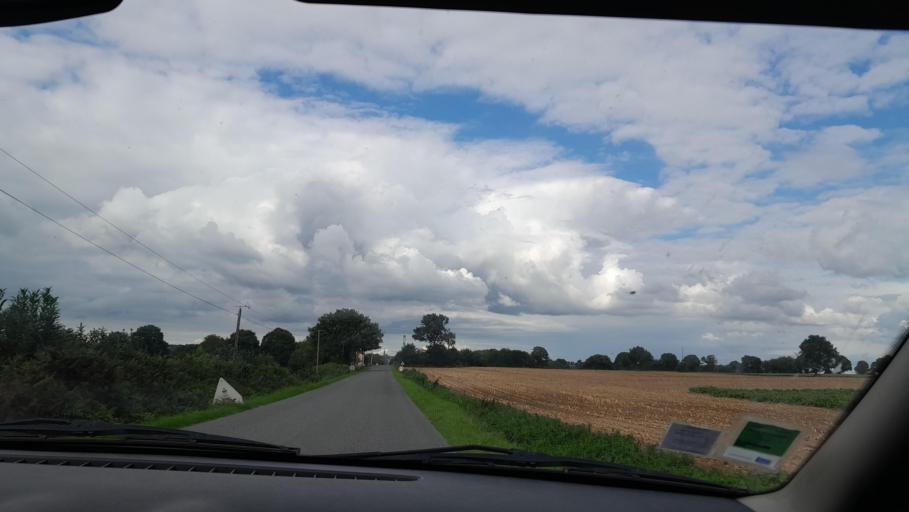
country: FR
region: Brittany
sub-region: Departement d'Ille-et-Vilaine
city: Le Pertre
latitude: 47.9846
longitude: -1.0413
